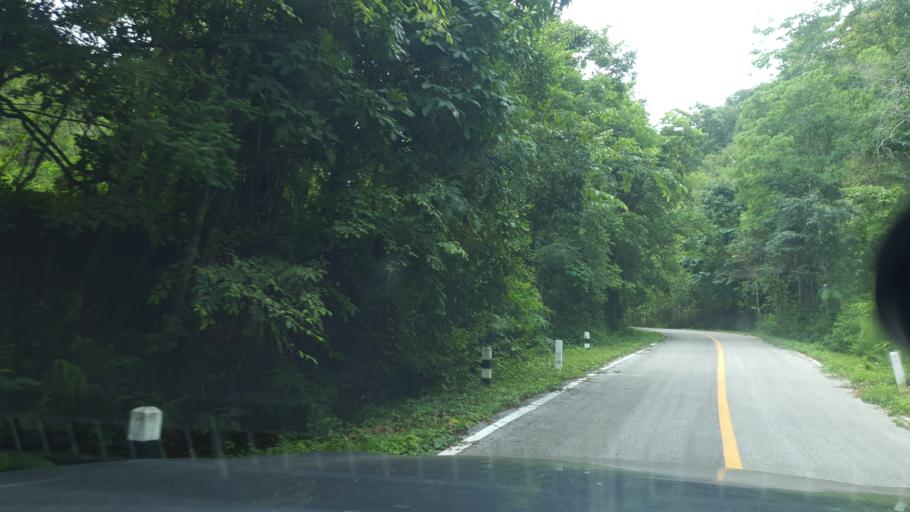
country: TH
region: Lamphun
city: Mae Tha
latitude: 18.4940
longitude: 99.2675
